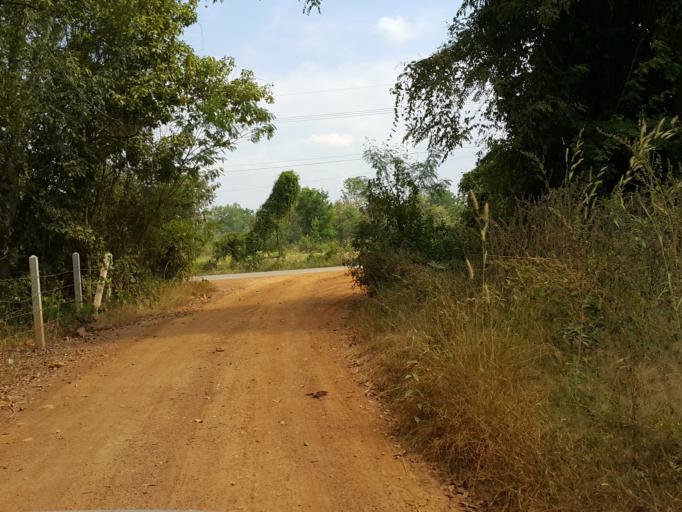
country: TH
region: Sukhothai
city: Thung Saliam
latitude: 17.3575
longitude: 99.5932
